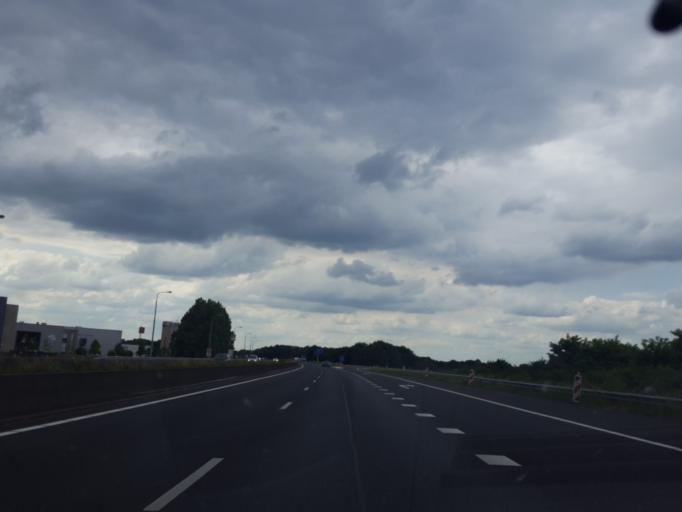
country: NL
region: Limburg
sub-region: Gemeente Venlo
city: Venlo
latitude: 51.3945
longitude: 6.1816
